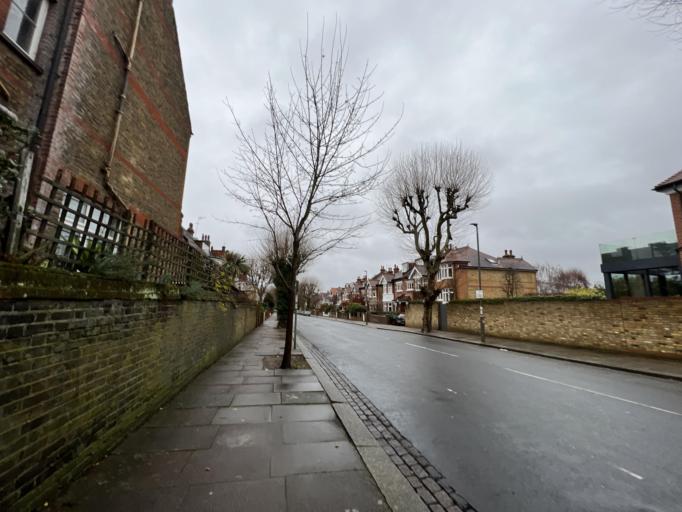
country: GB
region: England
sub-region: Greater London
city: Wandsworth
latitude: 51.4594
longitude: -0.2299
